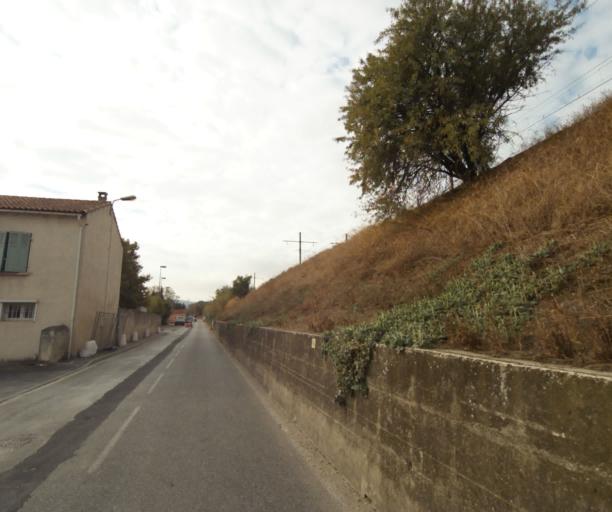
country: FR
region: Provence-Alpes-Cote d'Azur
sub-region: Departement des Bouches-du-Rhone
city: Saint-Victoret
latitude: 43.4154
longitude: 5.2521
